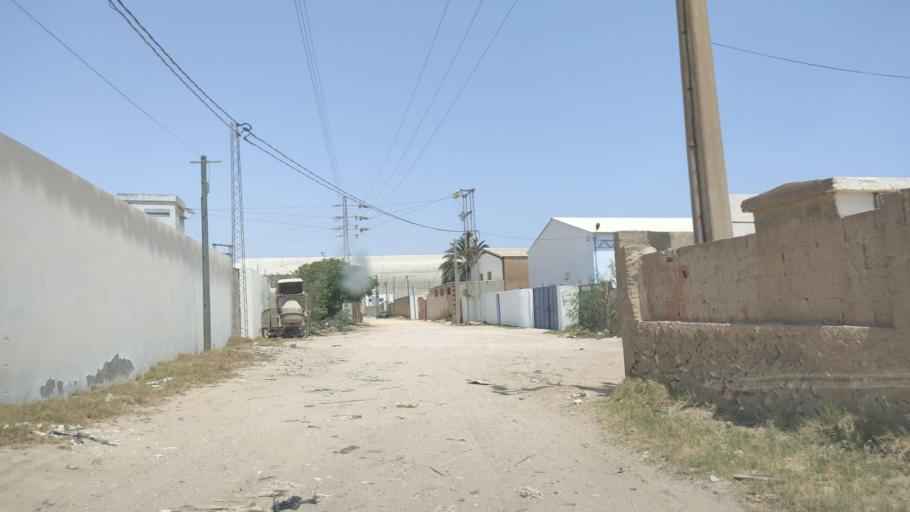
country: TN
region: Safaqis
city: Sfax
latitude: 34.6923
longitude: 10.7230
